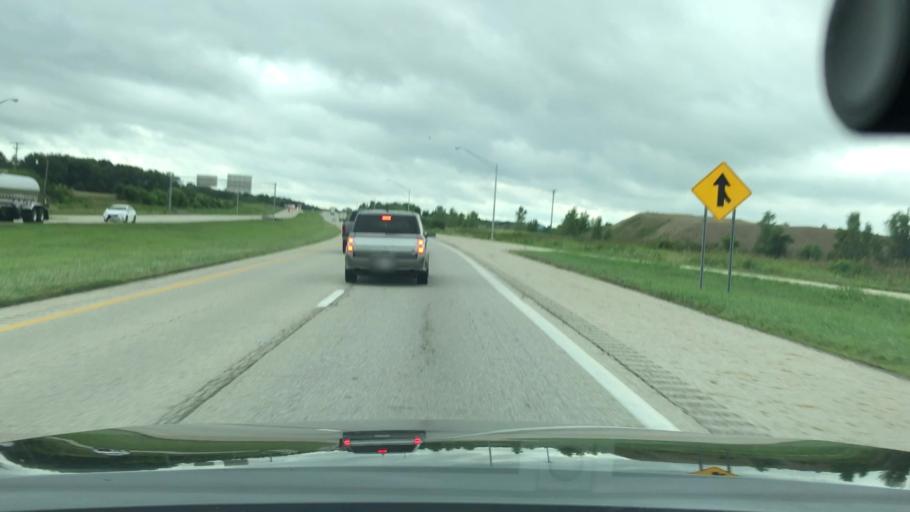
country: US
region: Ohio
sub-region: Ross County
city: Chillicothe
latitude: 39.2978
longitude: -82.9089
